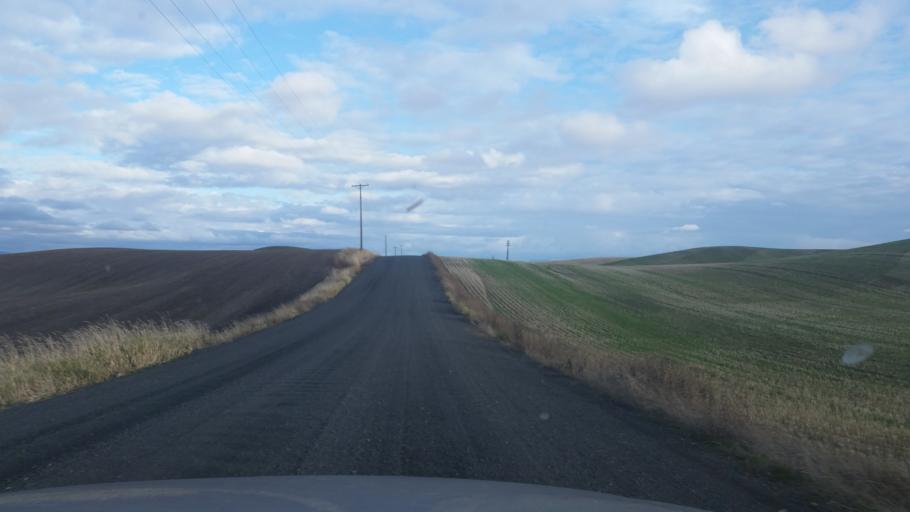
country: US
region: Washington
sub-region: Spokane County
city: Cheney
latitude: 47.4273
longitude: -117.4063
